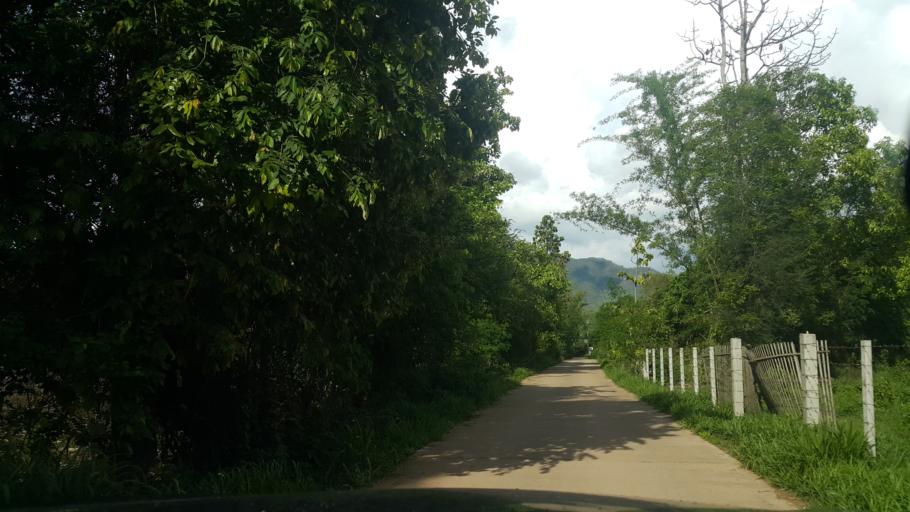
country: TH
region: Chiang Mai
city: Mae On
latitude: 18.7176
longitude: 99.2125
